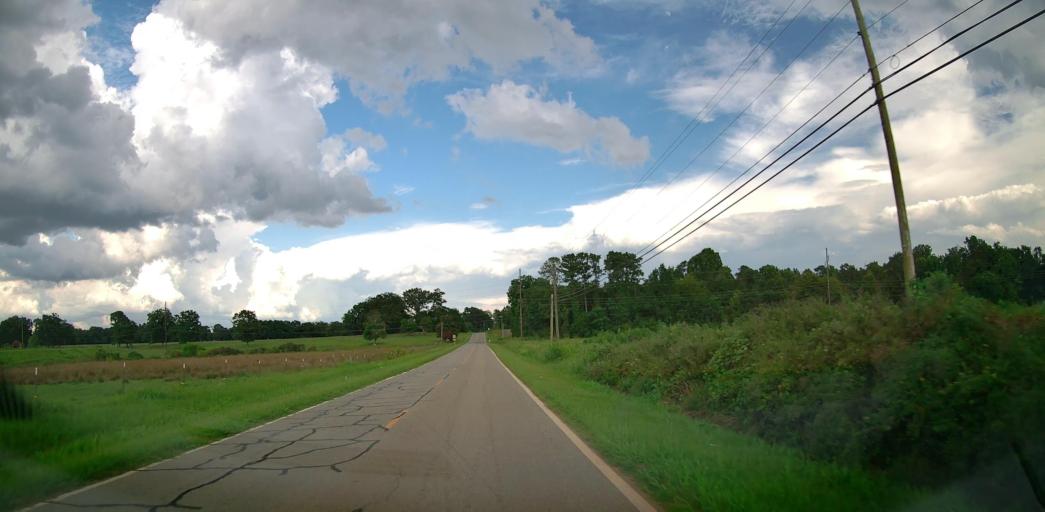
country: US
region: Georgia
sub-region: Bleckley County
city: Cochran
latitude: 32.3955
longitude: -83.3679
